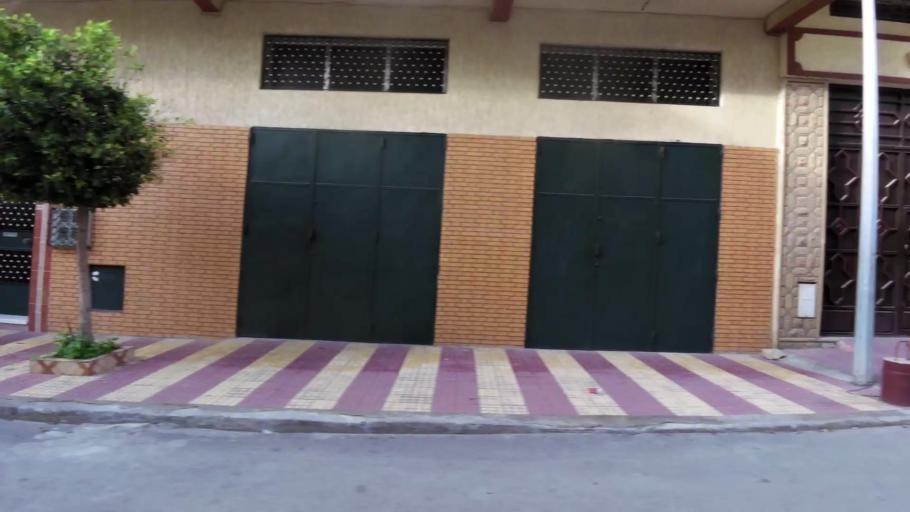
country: MA
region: Tanger-Tetouan
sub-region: Tanger-Assilah
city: Tangier
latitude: 35.7625
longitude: -5.8370
